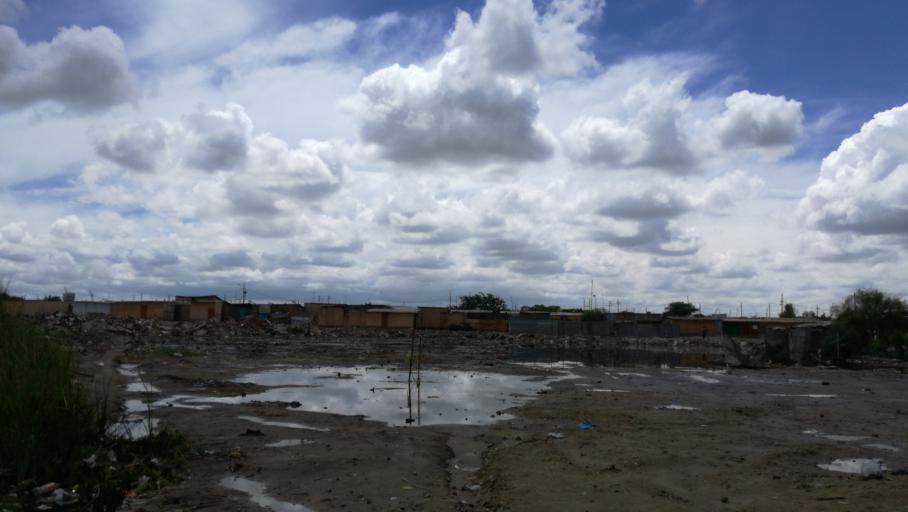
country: PE
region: Piura
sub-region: Provincia de Piura
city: Piura
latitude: -5.2054
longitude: -80.6559
